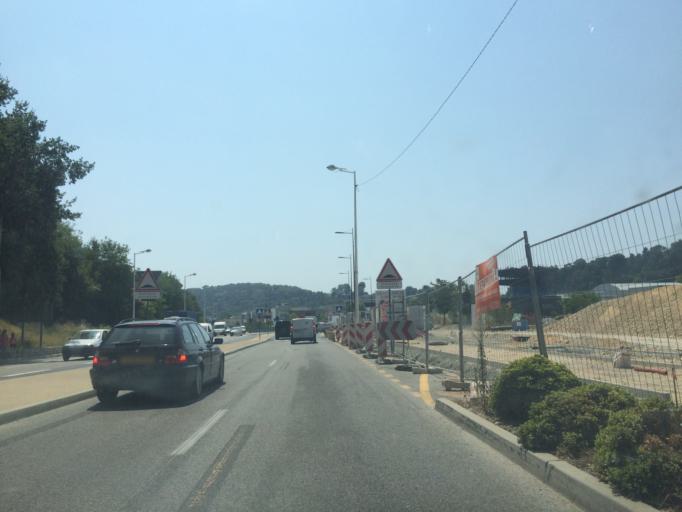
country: FR
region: Provence-Alpes-Cote d'Azur
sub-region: Departement des Alpes-Maritimes
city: Villeneuve-Loubet
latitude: 43.6666
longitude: 7.1275
